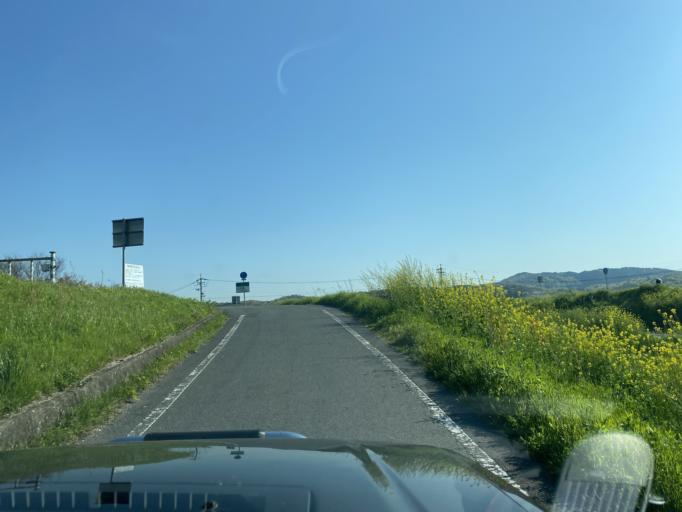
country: JP
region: Kyoto
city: Tanabe
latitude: 34.8309
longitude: 135.7653
